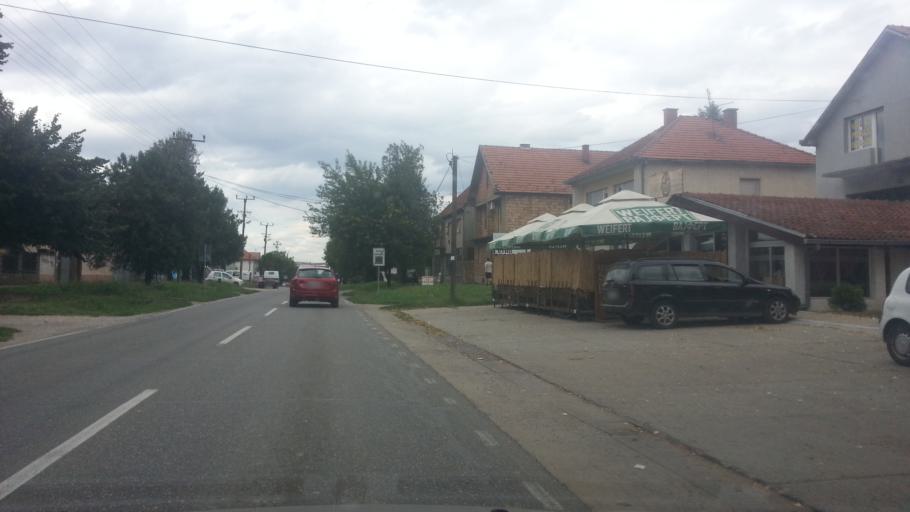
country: RS
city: Novi Banovci
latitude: 44.9583
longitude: 20.2809
